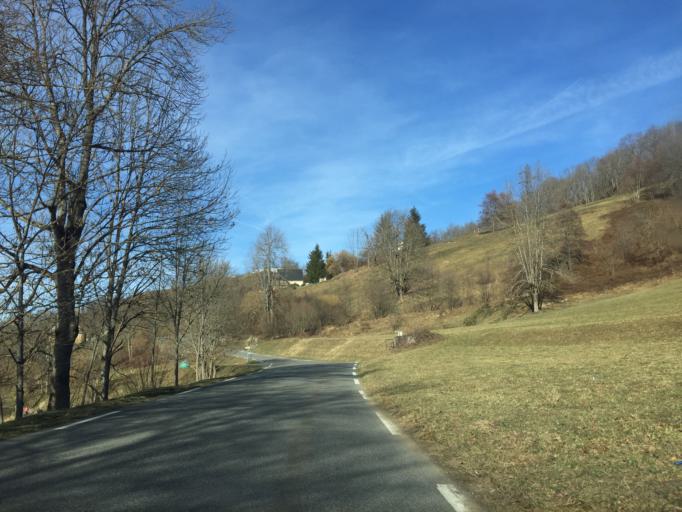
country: FR
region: Midi-Pyrenees
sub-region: Departement des Hautes-Pyrenees
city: Saint-Lary-Soulan
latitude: 42.8030
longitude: 0.4113
